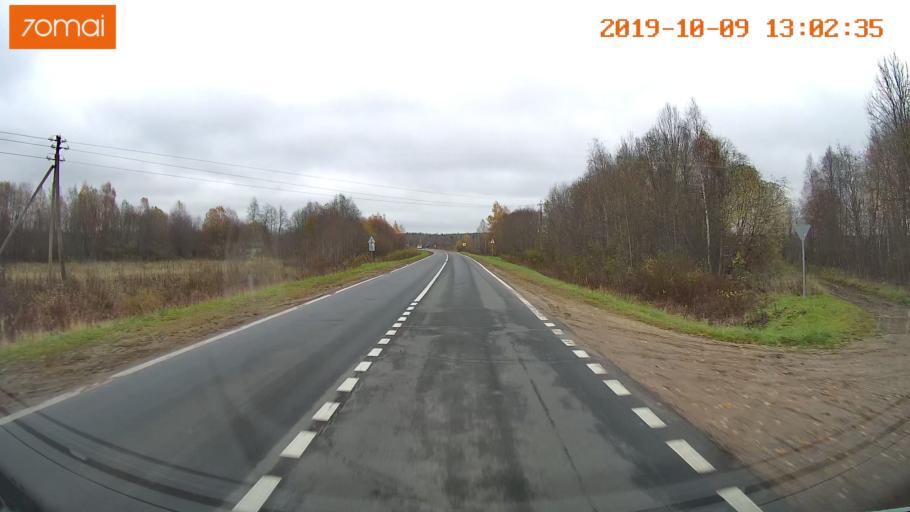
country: RU
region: Jaroslavl
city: Prechistoye
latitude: 58.3606
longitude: 40.5050
